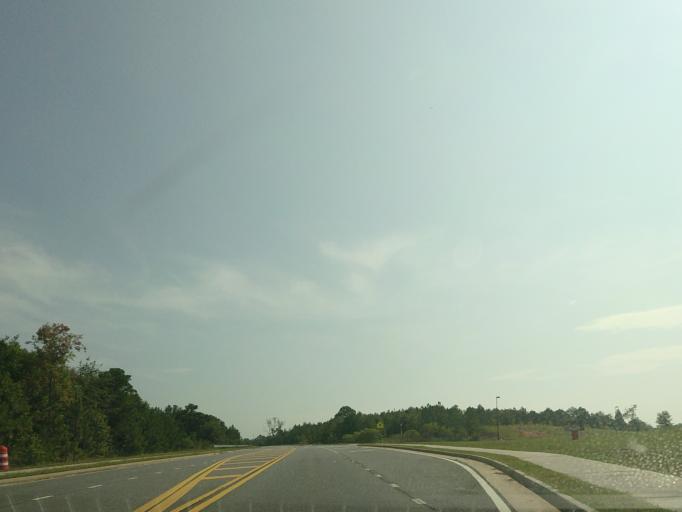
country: US
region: Georgia
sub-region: Peach County
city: Byron
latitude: 32.7387
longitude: -83.7167
